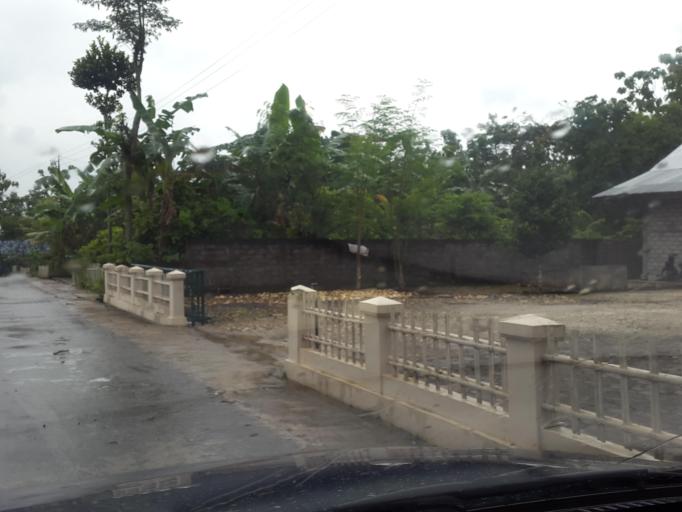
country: ID
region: Daerah Istimewa Yogyakarta
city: Wonosari
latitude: -7.9591
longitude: 110.6383
